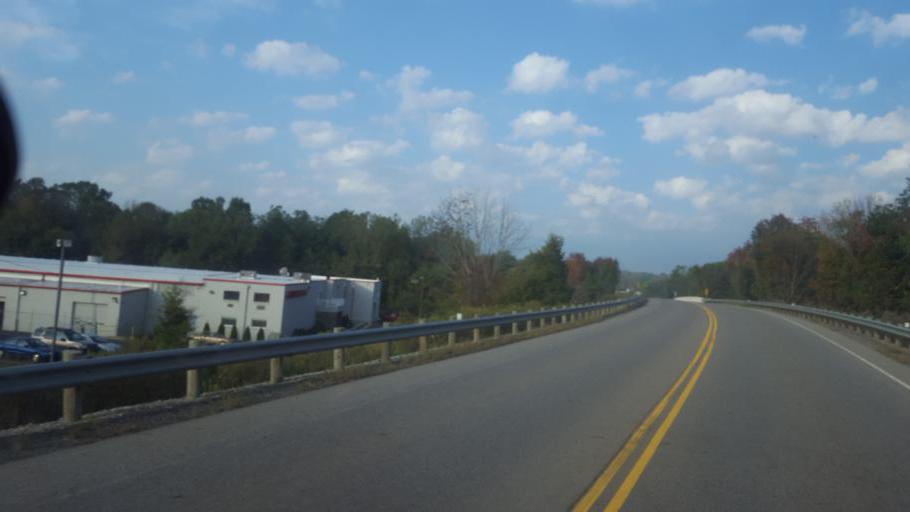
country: US
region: Ohio
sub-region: Licking County
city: Utica
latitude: 40.2313
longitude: -82.4447
